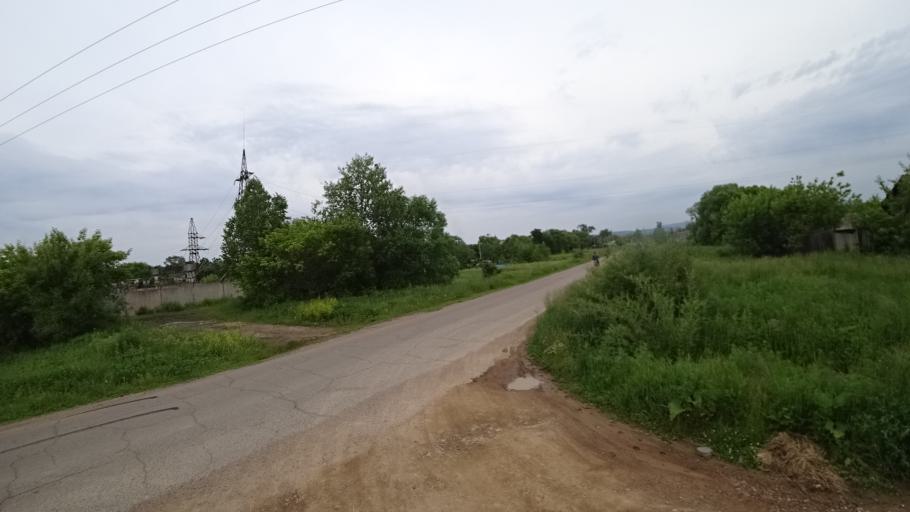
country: RU
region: Primorskiy
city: Novosysoyevka
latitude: 44.2341
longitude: 133.3704
